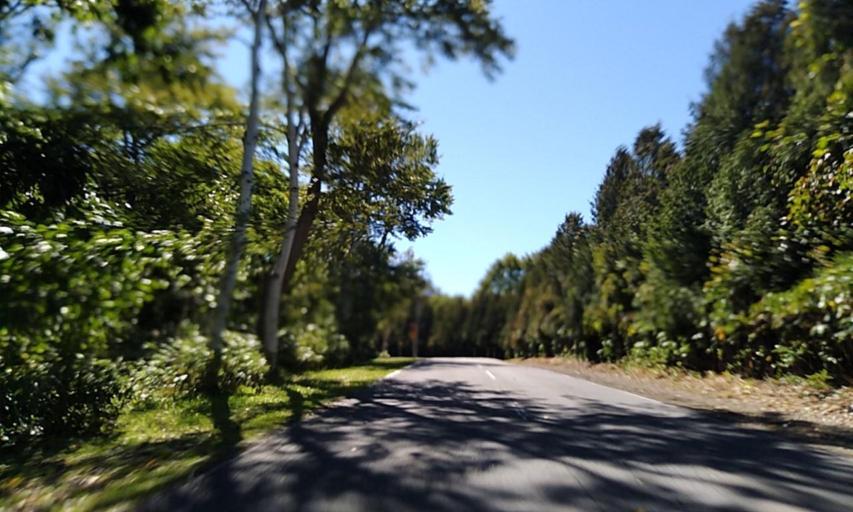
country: JP
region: Hokkaido
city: Sapporo
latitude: 42.9988
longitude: 141.3924
